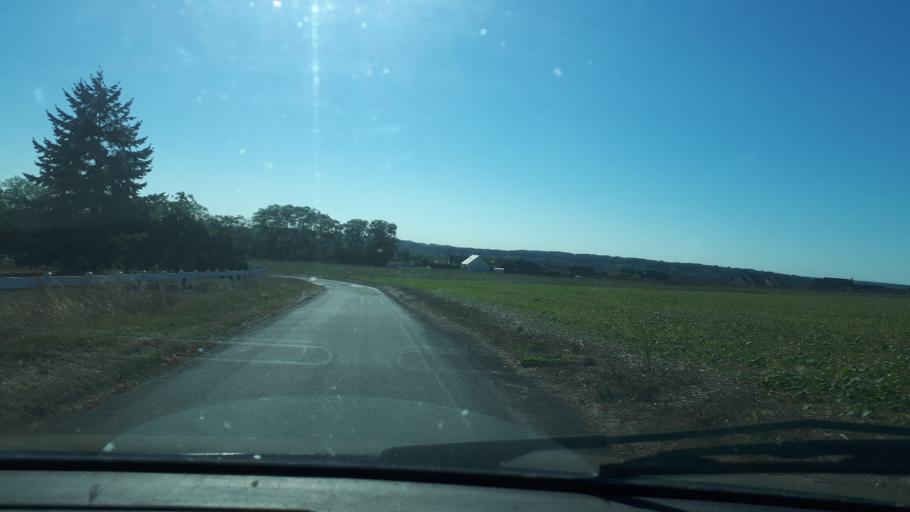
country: FR
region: Centre
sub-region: Departement du Loir-et-Cher
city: Naveil
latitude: 47.7970
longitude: 1.0197
